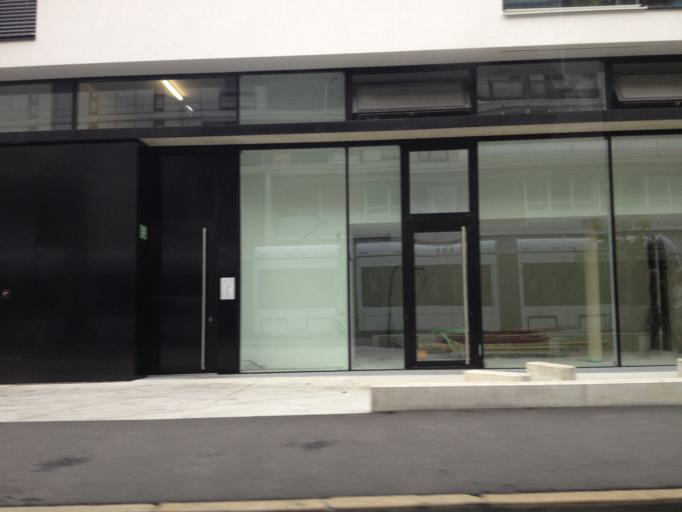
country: AT
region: Styria
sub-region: Graz Stadt
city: Graz
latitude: 47.0801
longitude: 15.4330
